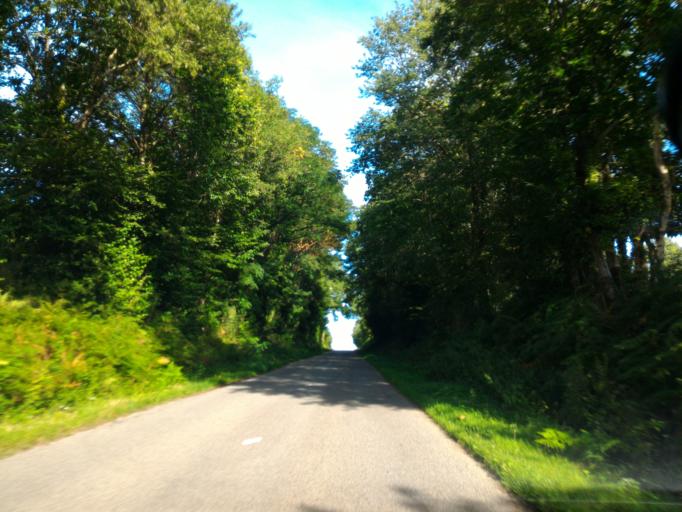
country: FR
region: Poitou-Charentes
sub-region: Departement de la Charente
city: Brigueuil
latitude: 45.9974
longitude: 0.8693
